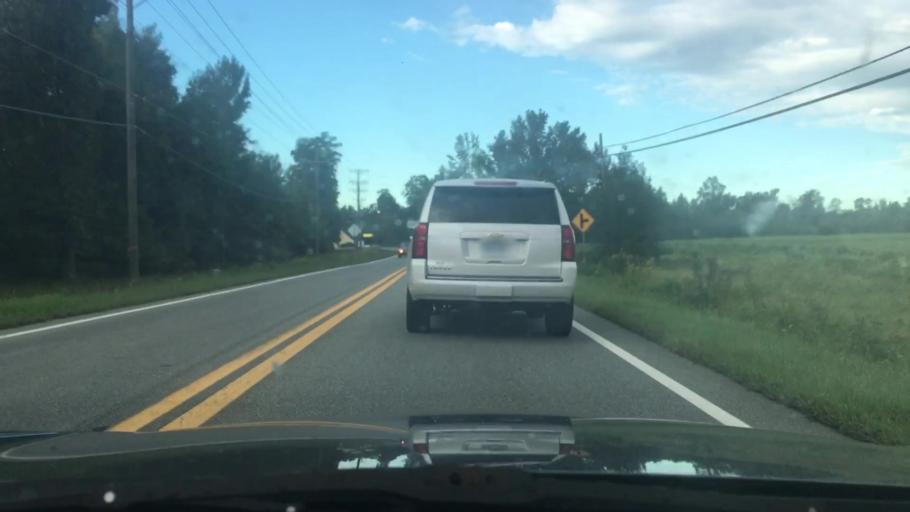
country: US
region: North Carolina
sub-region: Alamance County
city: Green Level
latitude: 36.1411
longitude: -79.3436
